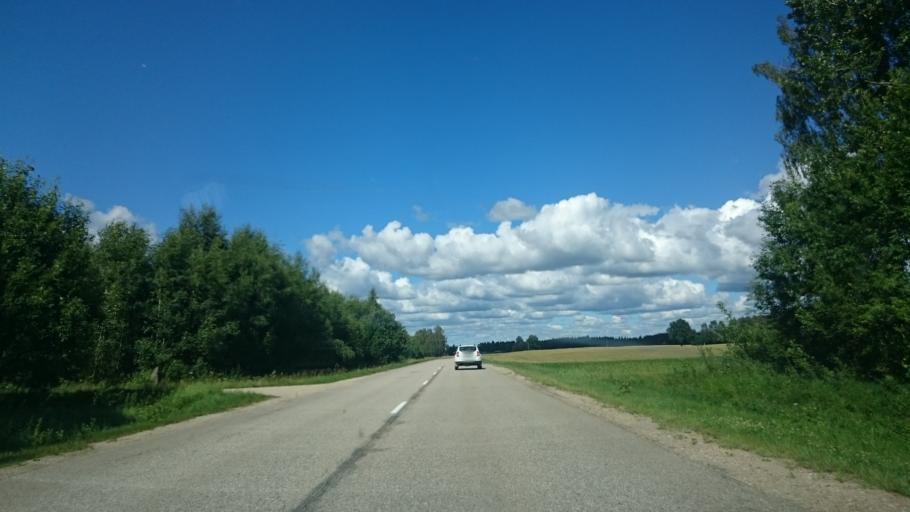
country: LV
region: Kuldigas Rajons
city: Kuldiga
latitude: 56.8907
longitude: 21.8844
